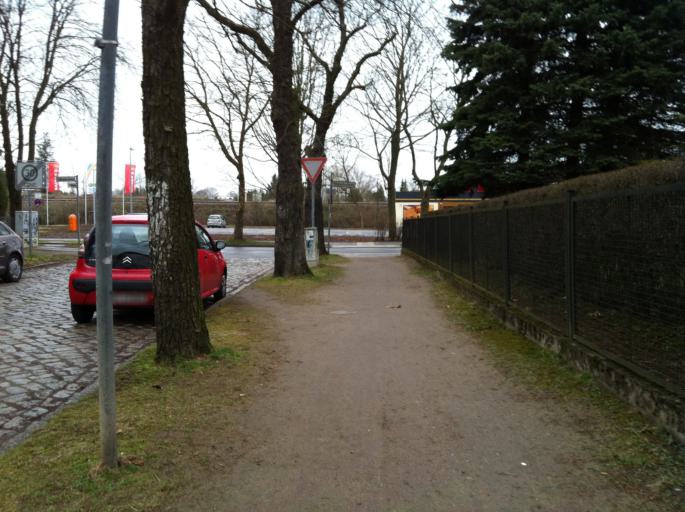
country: DE
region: Berlin
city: Karow
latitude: 52.6159
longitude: 13.4722
